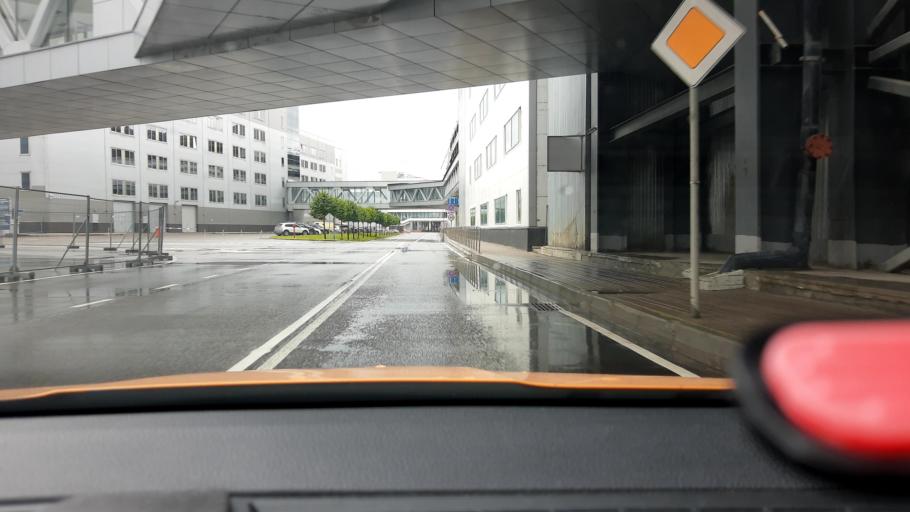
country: RU
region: Moscow
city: Strogino
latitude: 55.8262
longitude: 37.3855
